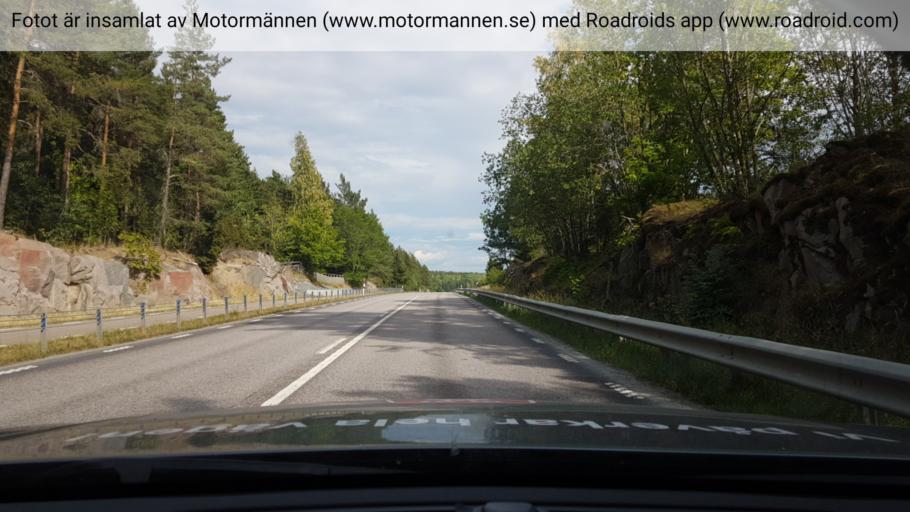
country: SE
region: Uppsala
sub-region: Uppsala Kommun
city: Uppsala
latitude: 59.8515
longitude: 17.4875
